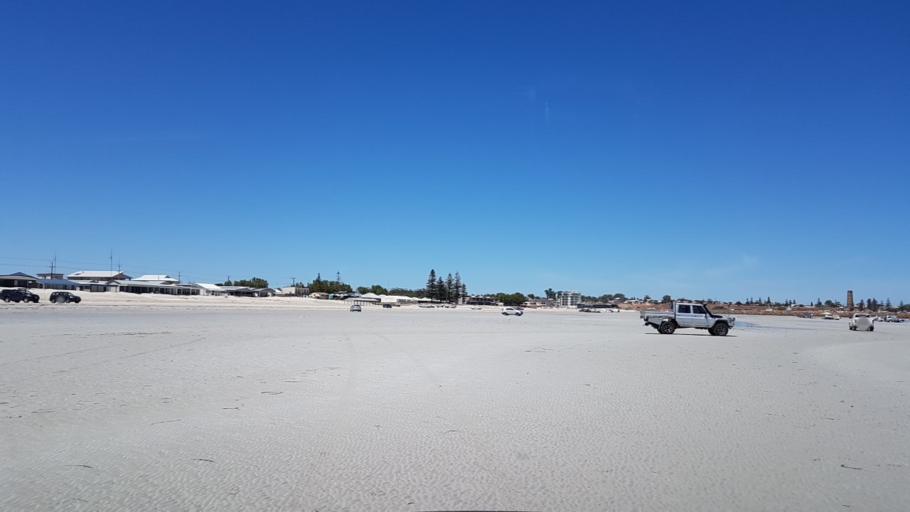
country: AU
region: South Australia
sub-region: Copper Coast
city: Wallaroo
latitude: -33.9154
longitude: 137.6302
